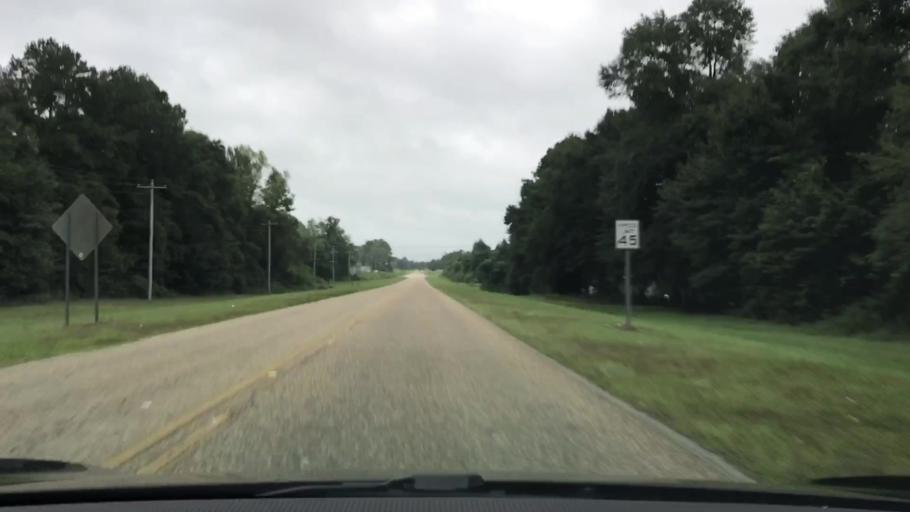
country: US
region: Alabama
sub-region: Coffee County
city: Elba
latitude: 31.4071
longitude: -86.0823
